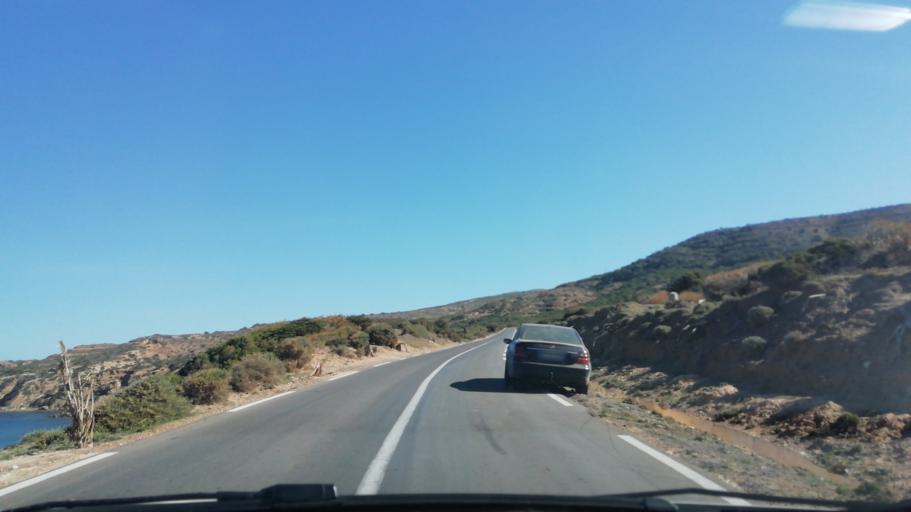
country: DZ
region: Ain Temouchent
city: El Amria
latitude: 35.6427
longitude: -1.0577
